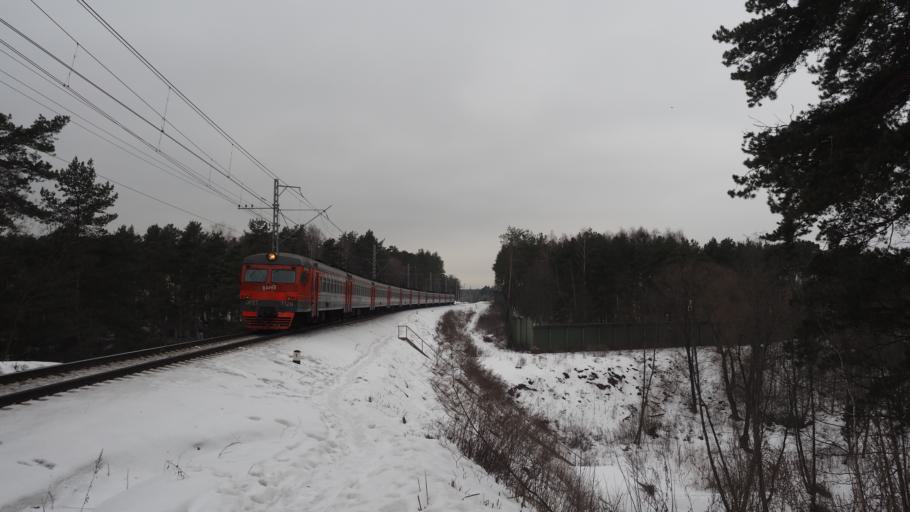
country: RU
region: Moskovskaya
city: Barvikha
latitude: 55.7370
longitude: 37.2759
